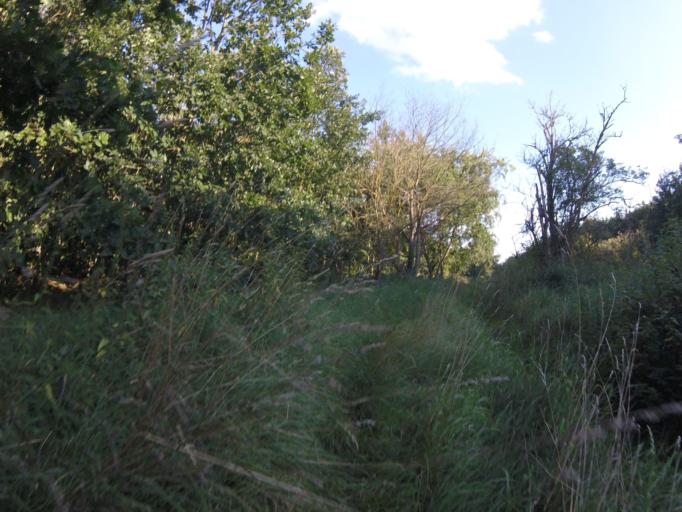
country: DE
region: Brandenburg
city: Schulzendorf
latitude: 52.3164
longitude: 13.5594
